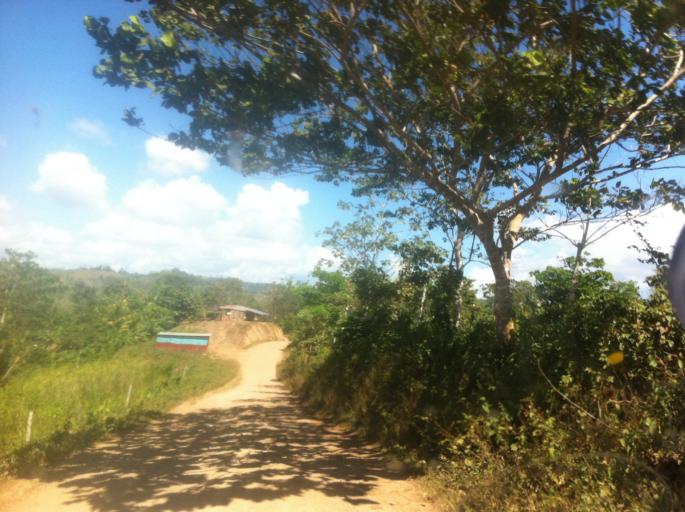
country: CR
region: Alajuela
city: Los Chiles
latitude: 11.2490
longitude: -84.4488
